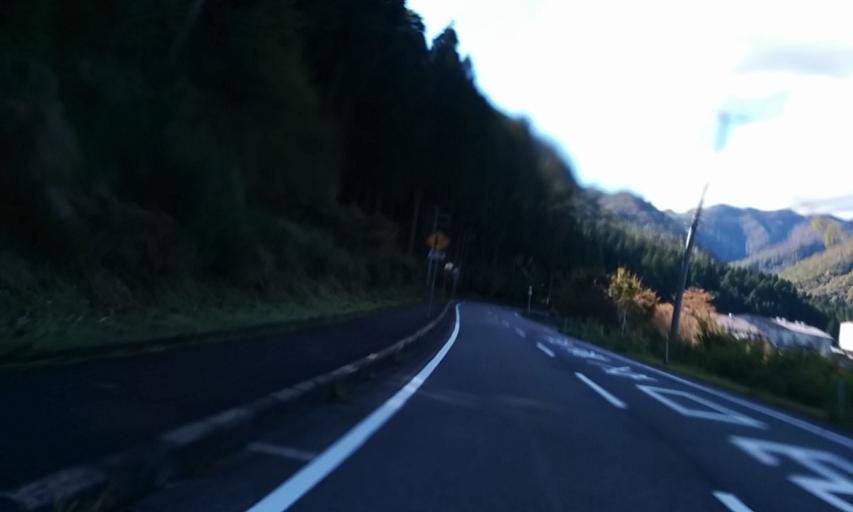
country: JP
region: Kyoto
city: Kameoka
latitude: 35.2603
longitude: 135.5570
